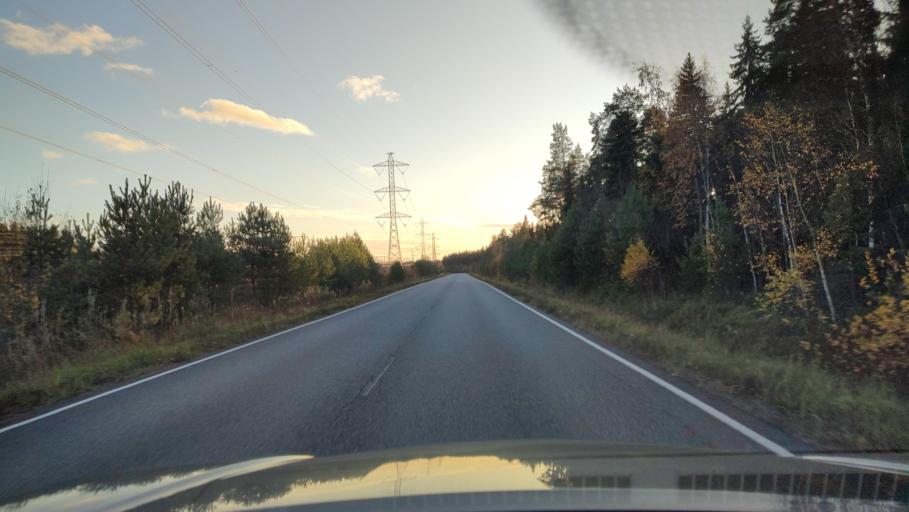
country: FI
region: Ostrobothnia
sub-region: Sydosterbotten
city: Kristinestad
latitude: 62.2869
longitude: 21.3575
